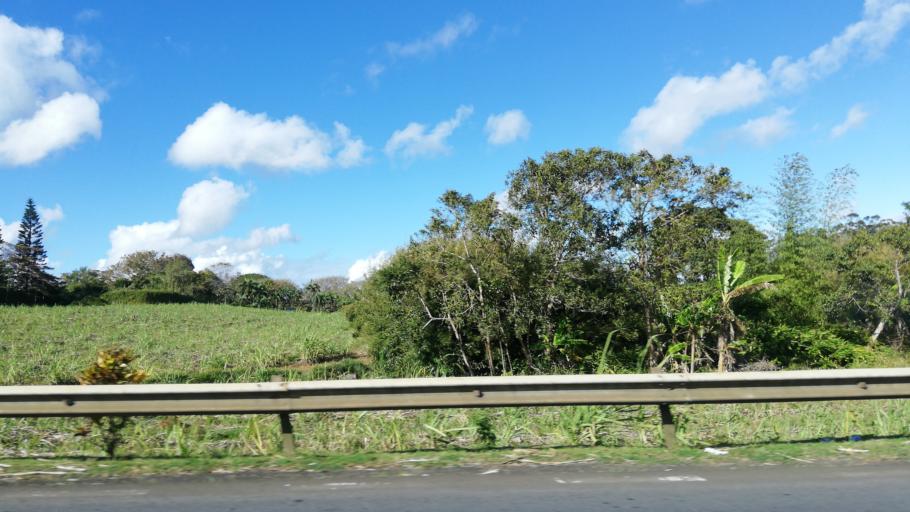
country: MU
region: Moka
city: Quartier Militaire
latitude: -20.2355
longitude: 57.5727
